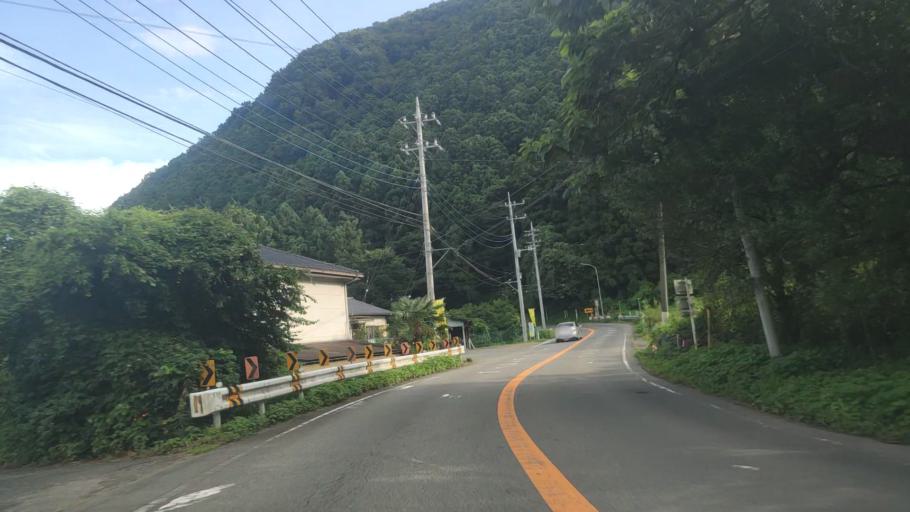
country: JP
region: Gunma
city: Omamacho-omama
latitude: 36.4583
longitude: 139.2640
